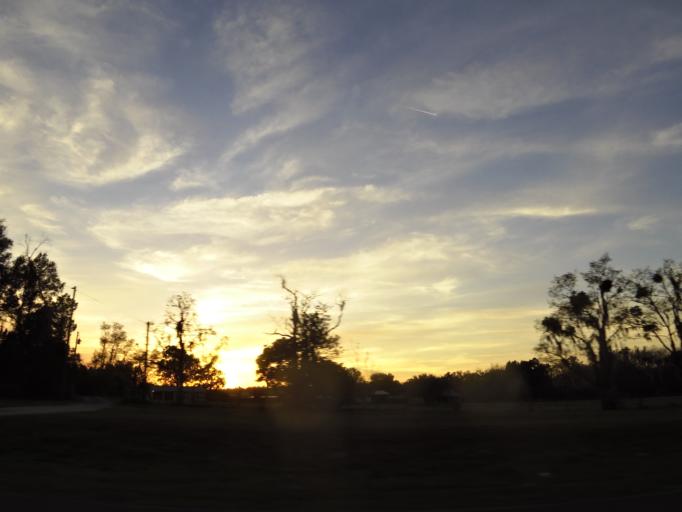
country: US
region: Florida
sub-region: Volusia County
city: De Leon Springs
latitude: 29.1308
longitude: -81.2852
